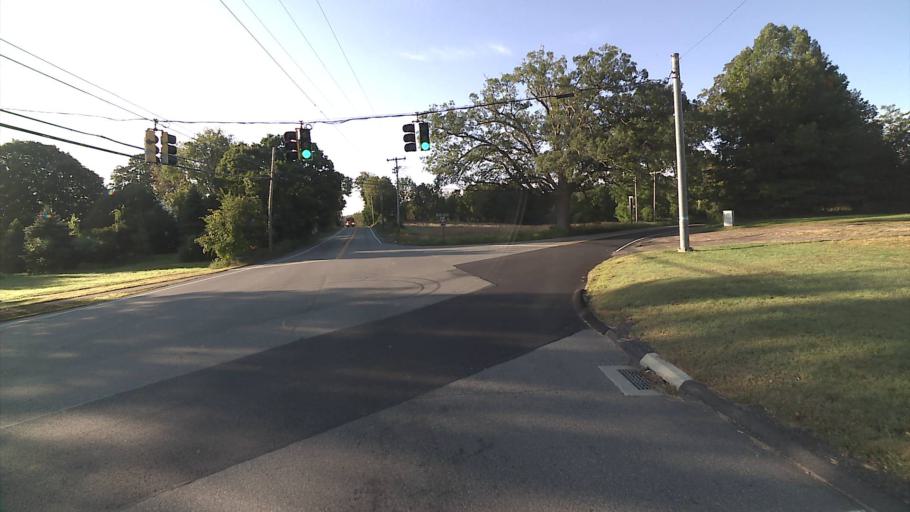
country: US
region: Connecticut
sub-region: Tolland County
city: South Coventry
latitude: 41.8041
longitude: -72.3030
